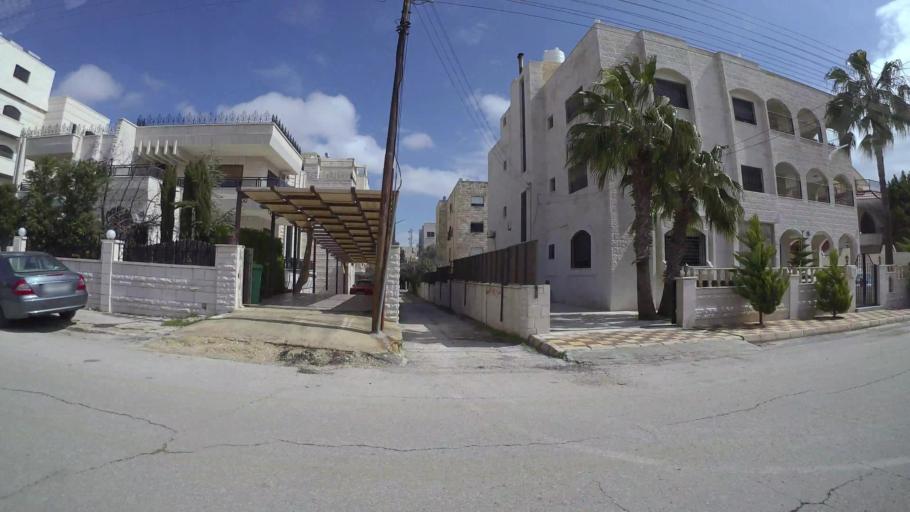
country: JO
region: Amman
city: Wadi as Sir
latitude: 31.9641
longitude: 35.8404
